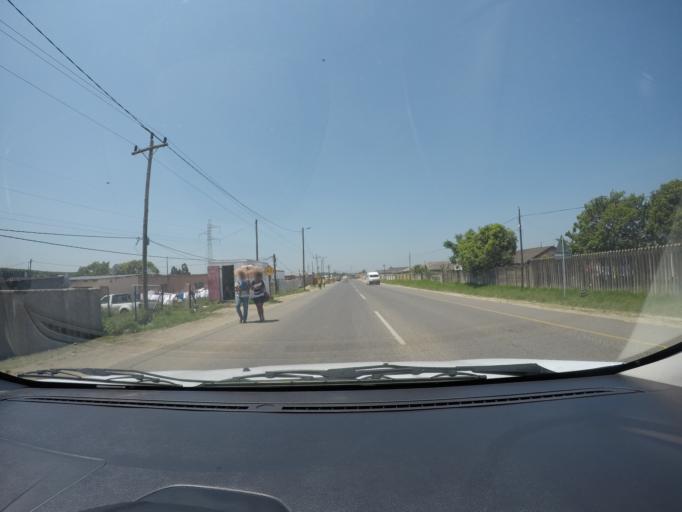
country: ZA
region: KwaZulu-Natal
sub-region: uThungulu District Municipality
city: eSikhawini
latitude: -28.8747
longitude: 31.8963
